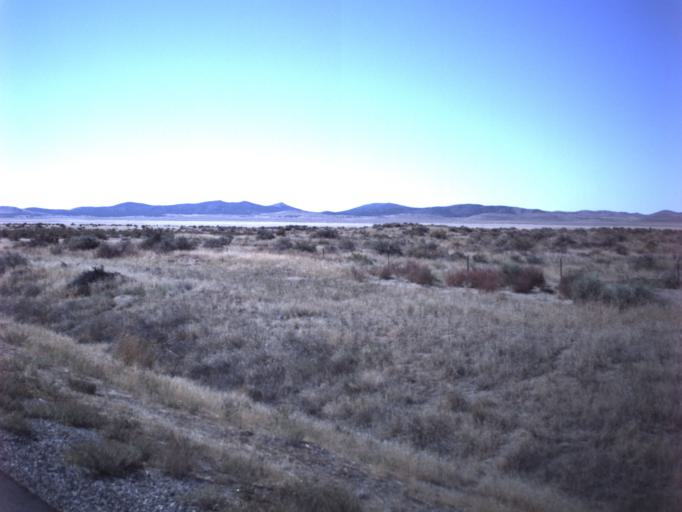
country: US
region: Utah
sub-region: Tooele County
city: Grantsville
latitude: 40.3263
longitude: -112.7441
